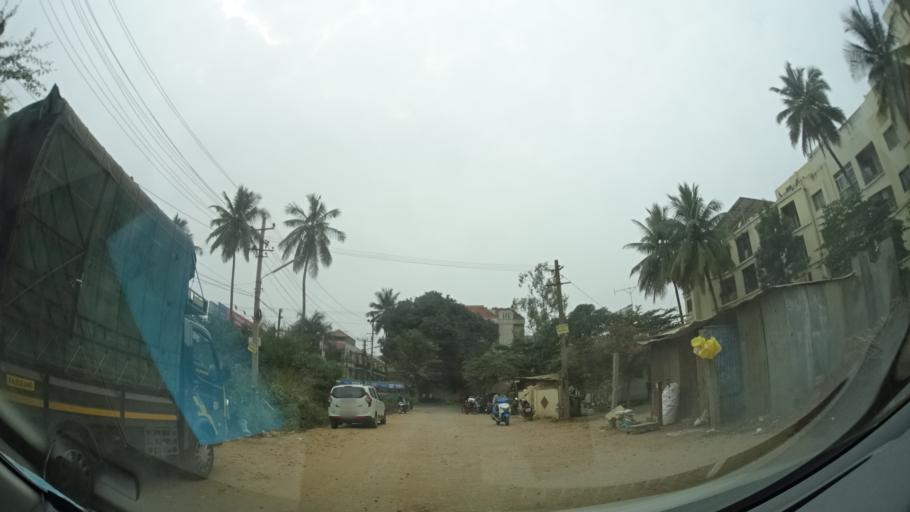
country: IN
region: Karnataka
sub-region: Bangalore Rural
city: Hoskote
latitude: 12.9574
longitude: 77.7421
